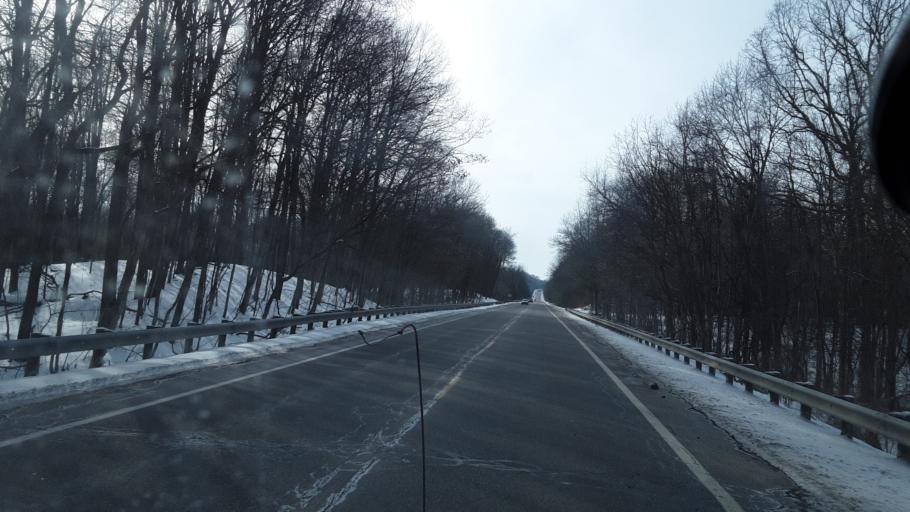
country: US
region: Ohio
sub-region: Summit County
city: Mogadore
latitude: 41.0272
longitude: -81.3570
